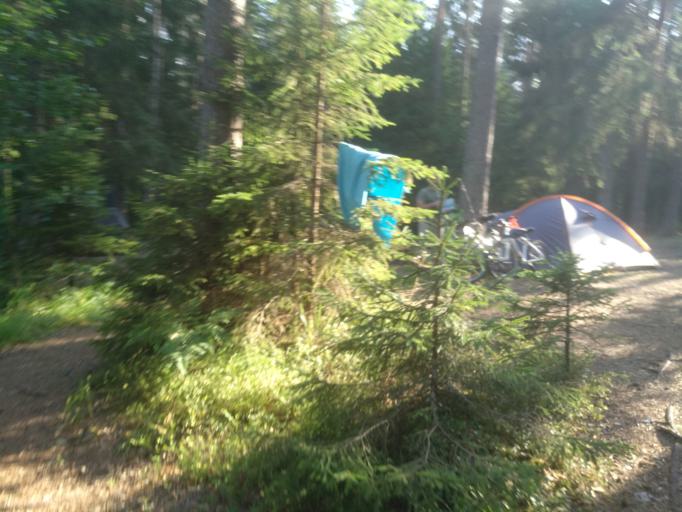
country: EE
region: Harju
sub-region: Loksa linn
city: Loksa
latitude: 59.3976
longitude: 25.6845
